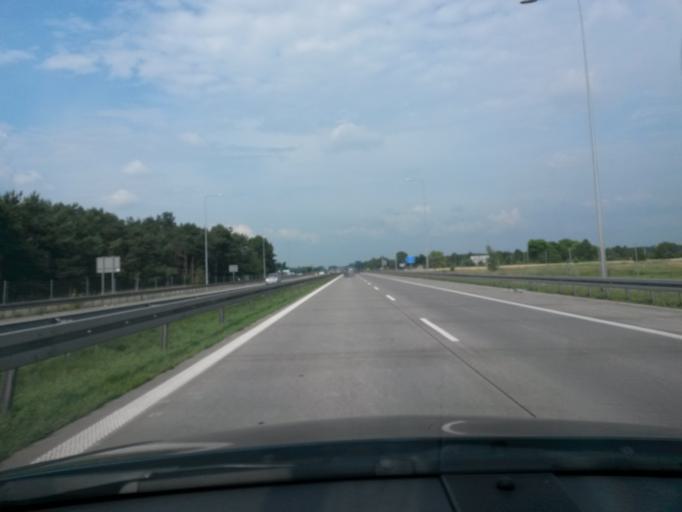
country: PL
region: Lodz Voivodeship
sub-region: Powiat piotrkowski
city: Wolborz
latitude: 51.5124
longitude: 19.9017
